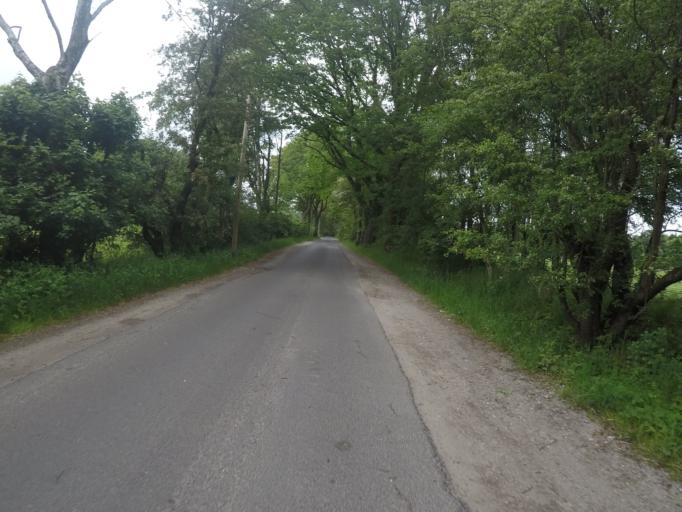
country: DE
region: Schleswig-Holstein
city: Bonningstedt
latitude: 53.6531
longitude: 9.9402
